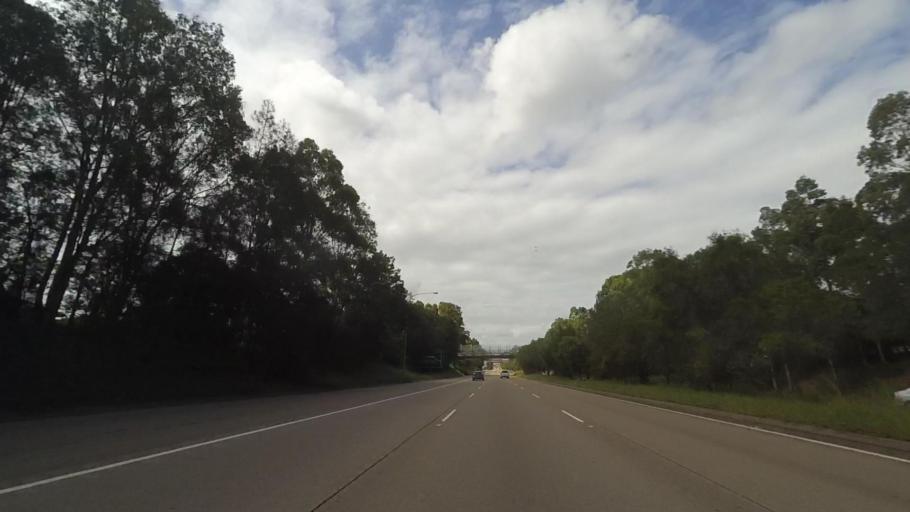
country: AU
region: New South Wales
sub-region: Newcastle
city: North Lambton
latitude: -32.9025
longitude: 151.6935
